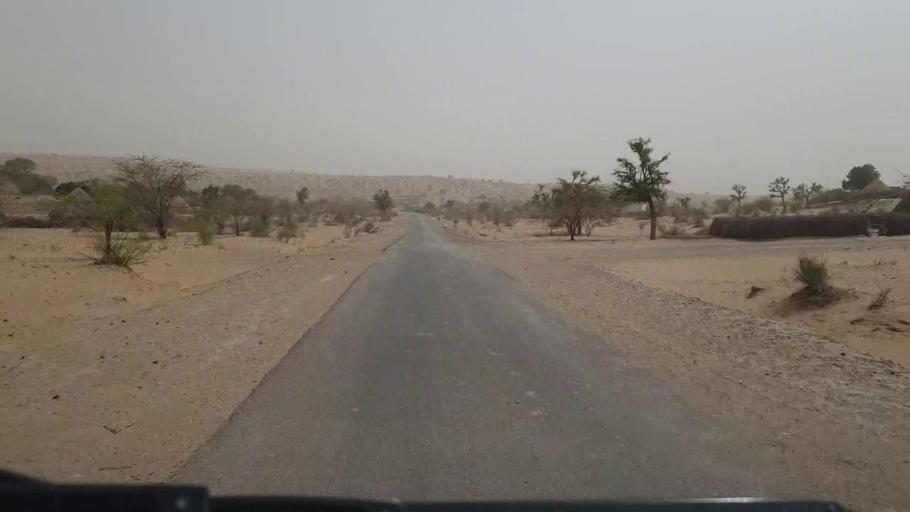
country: PK
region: Sindh
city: Islamkot
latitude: 25.2688
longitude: 70.6508
